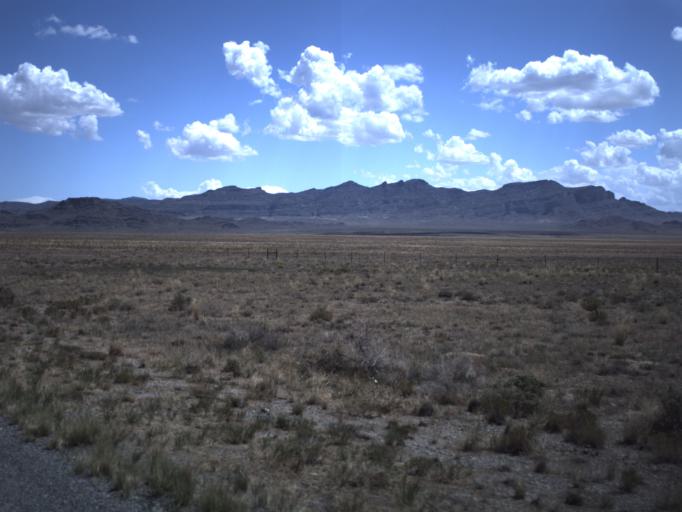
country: US
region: Utah
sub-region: Beaver County
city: Milford
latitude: 39.0514
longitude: -113.7815
